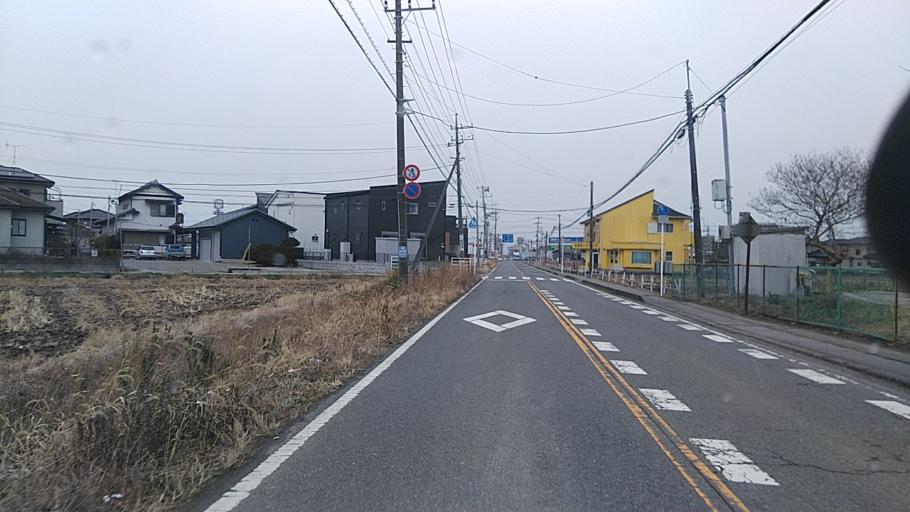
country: JP
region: Chiba
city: Togane
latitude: 35.5760
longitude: 140.3785
